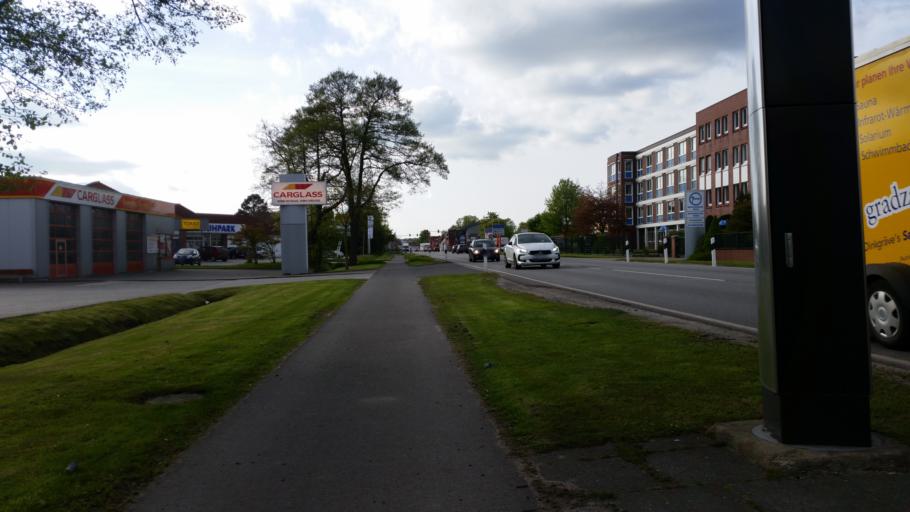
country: DE
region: Lower Saxony
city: Aurich
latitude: 53.4599
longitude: 7.4933
